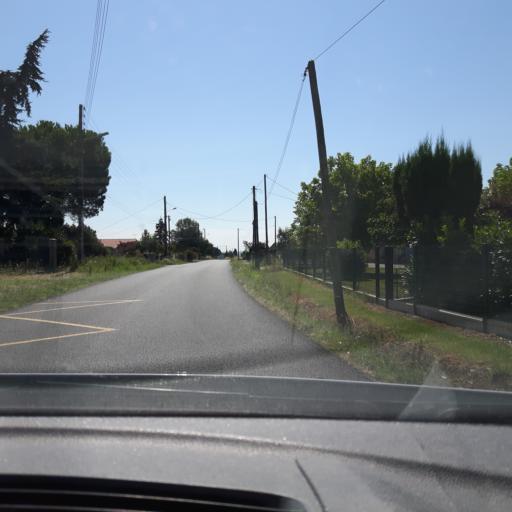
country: FR
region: Midi-Pyrenees
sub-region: Departement de la Haute-Garonne
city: Bouloc
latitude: 43.7862
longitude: 1.3959
